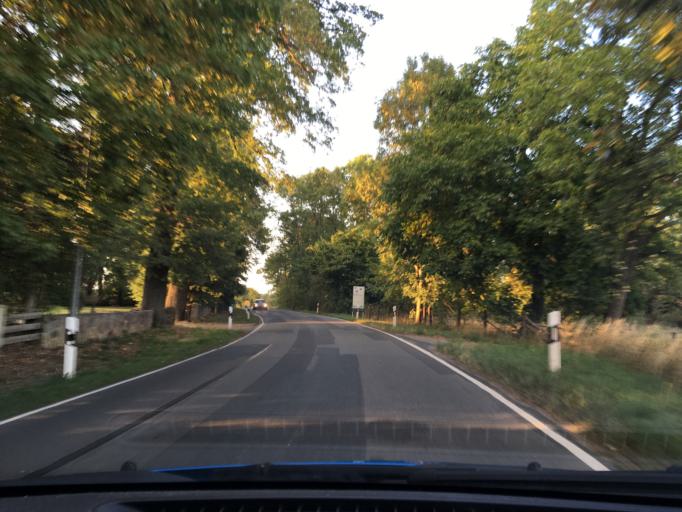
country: DE
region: Lower Saxony
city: Dahlem
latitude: 53.2289
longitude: 10.7559
